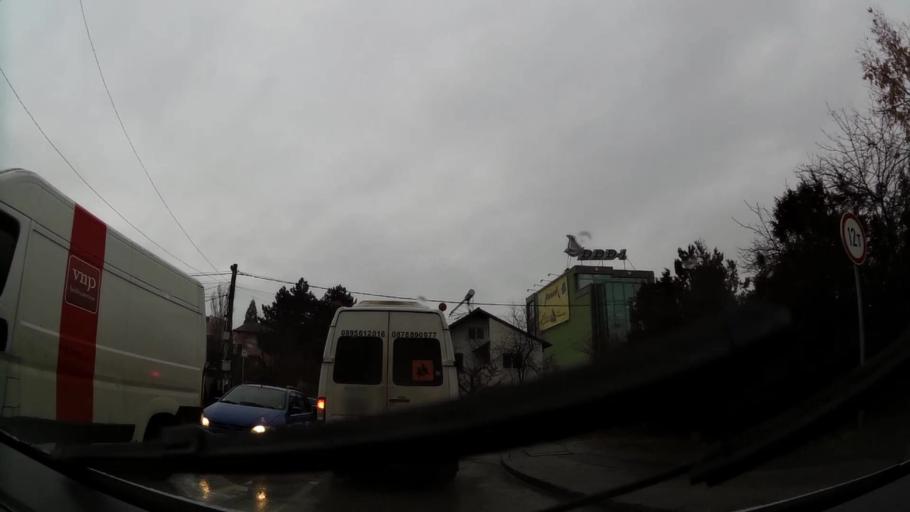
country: BG
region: Sofia-Capital
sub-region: Stolichna Obshtina
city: Sofia
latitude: 42.6457
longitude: 23.3338
